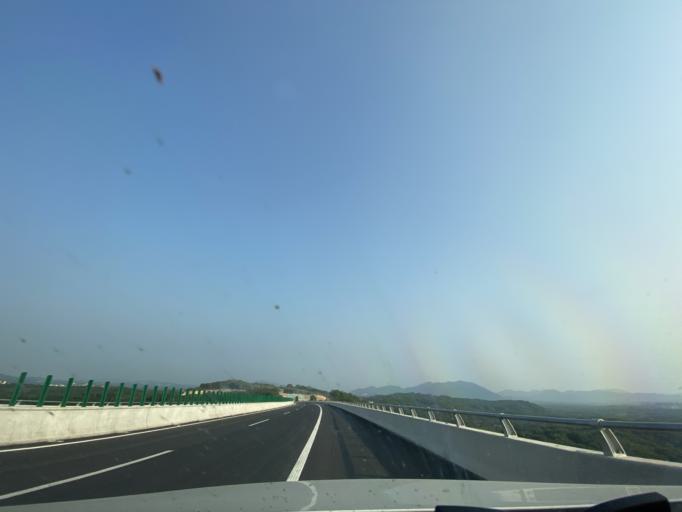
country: CN
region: Hainan
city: Xiangshui
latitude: 18.6352
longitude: 109.6315
